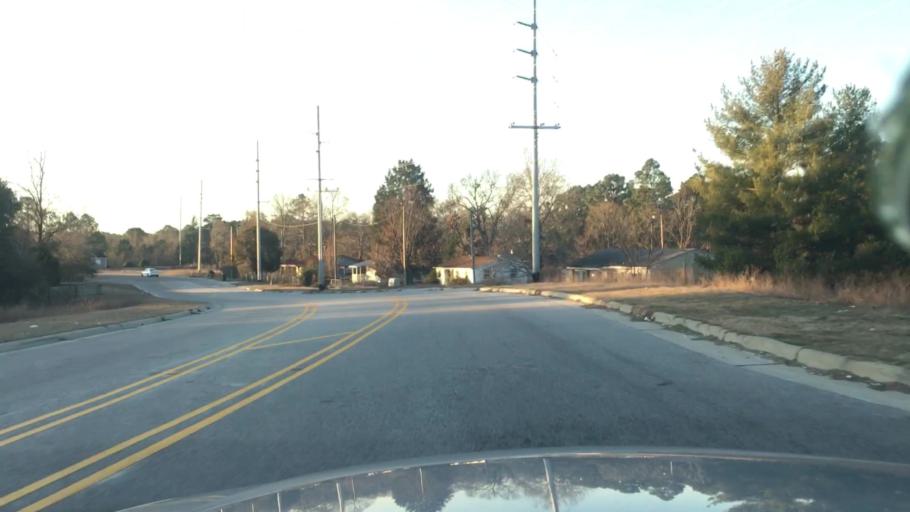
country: US
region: North Carolina
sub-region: Cumberland County
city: Hope Mills
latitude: 34.9981
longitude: -78.9342
